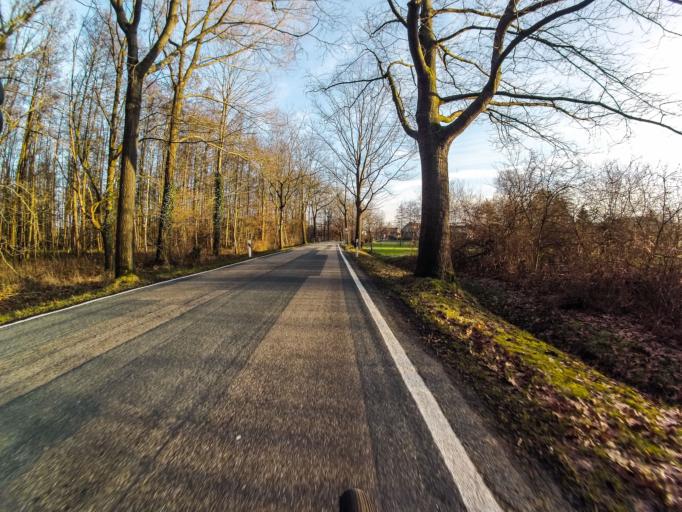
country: DE
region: North Rhine-Westphalia
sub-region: Regierungsbezirk Munster
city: Mettingen
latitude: 52.2979
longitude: 7.8220
